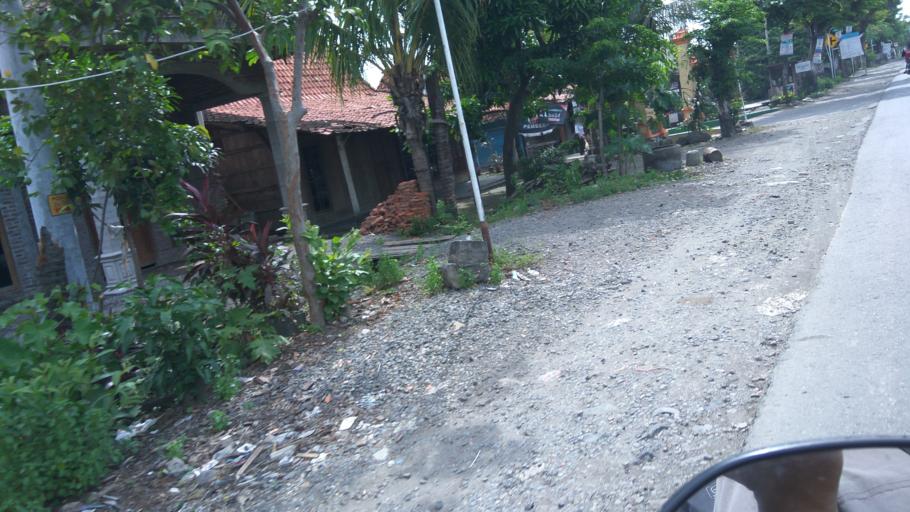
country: ID
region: Central Java
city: Mranggen
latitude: -7.0433
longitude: 110.5711
